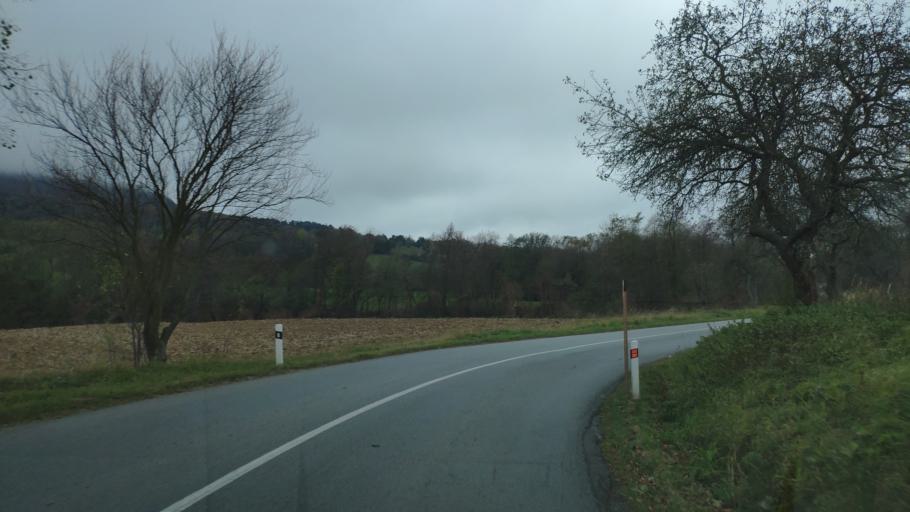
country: SK
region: Presovsky
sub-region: Okres Presov
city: Presov
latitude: 49.0983
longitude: 21.2367
